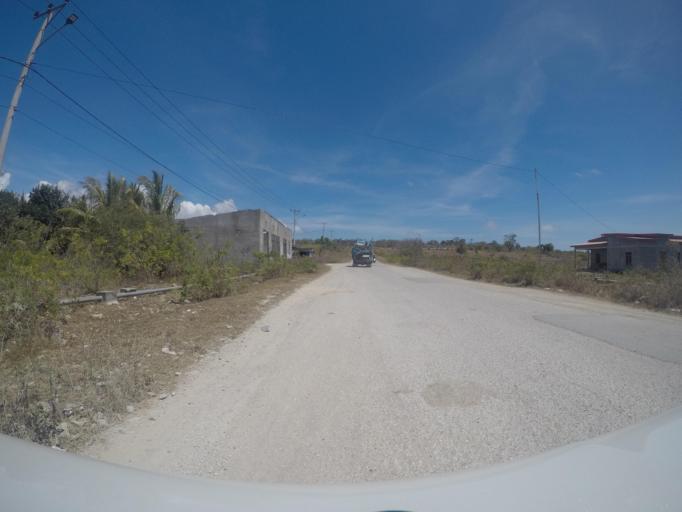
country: TL
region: Baucau
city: Baucau
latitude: -8.4709
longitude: 126.4386
